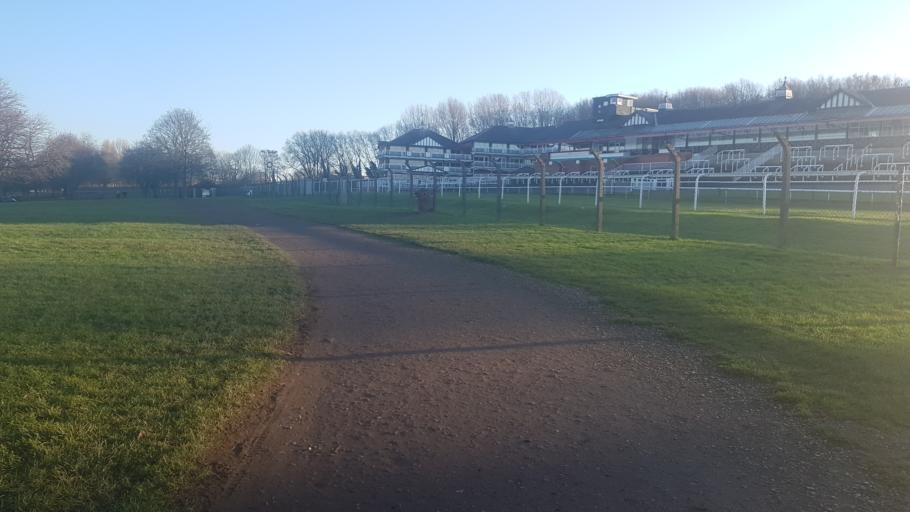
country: GB
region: England
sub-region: City and Borough of Wakefield
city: Pontefract
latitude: 53.6967
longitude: -1.3314
